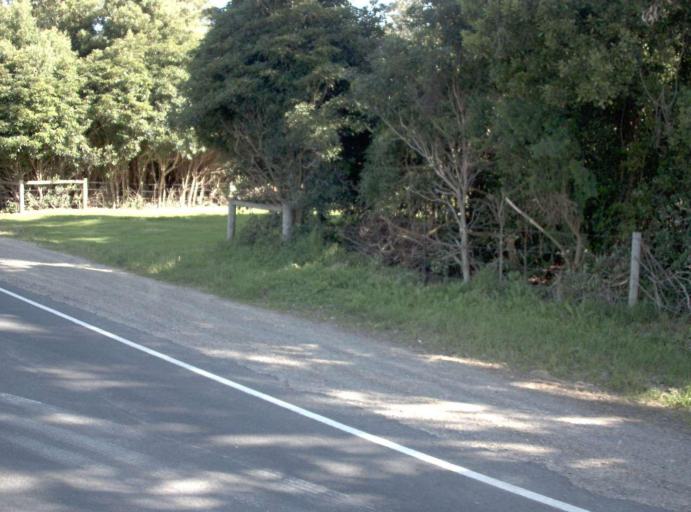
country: AU
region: Victoria
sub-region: East Gippsland
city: Lakes Entrance
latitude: -37.7540
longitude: 148.5239
